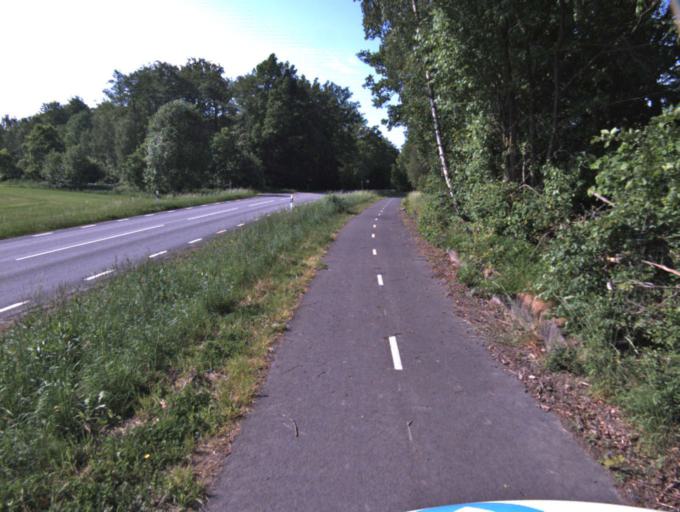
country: SE
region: Skane
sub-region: Kristianstads Kommun
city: Tollarp
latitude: 56.1494
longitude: 14.2608
